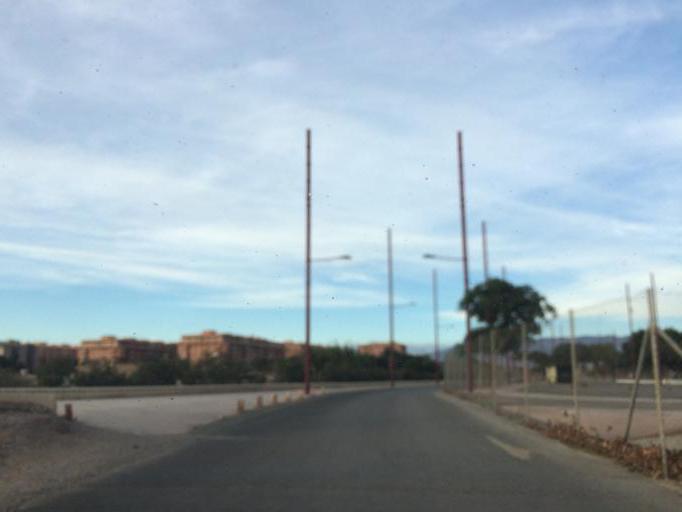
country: ES
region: Andalusia
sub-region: Provincia de Almeria
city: Almeria
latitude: 36.8327
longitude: -2.4324
